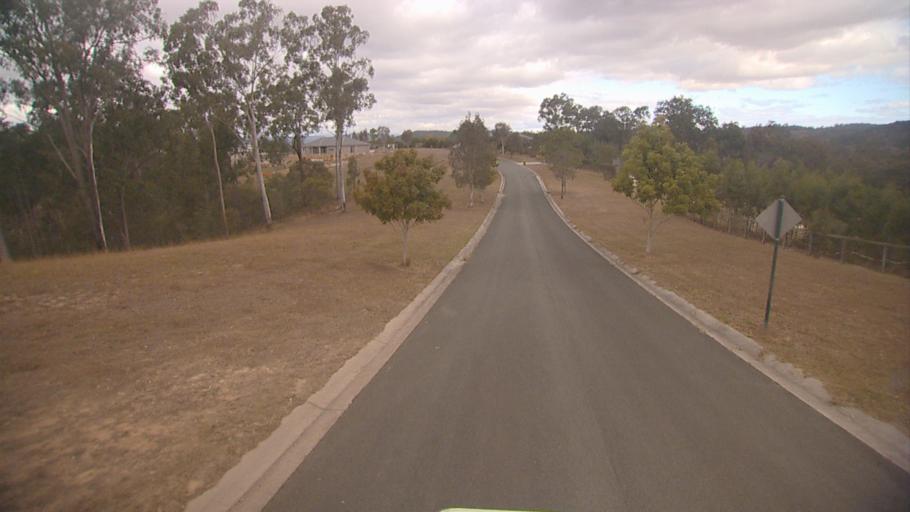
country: AU
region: Queensland
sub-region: Logan
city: Cedar Vale
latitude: -27.8694
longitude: 153.0716
